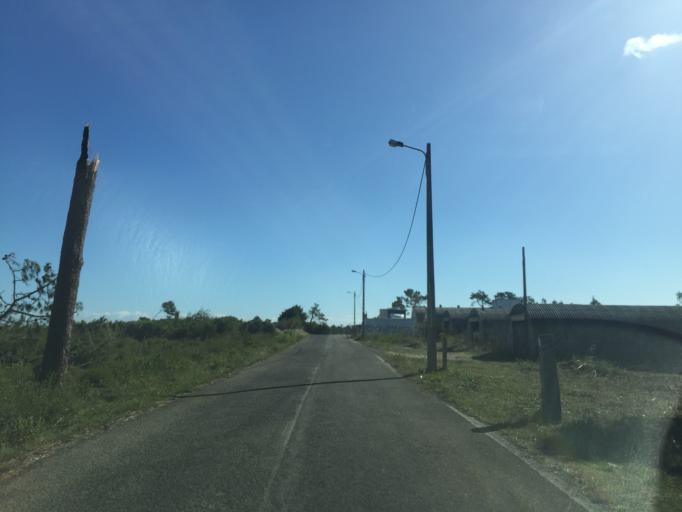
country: PT
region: Coimbra
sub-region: Figueira da Foz
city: Tavarede
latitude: 40.1951
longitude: -8.8479
